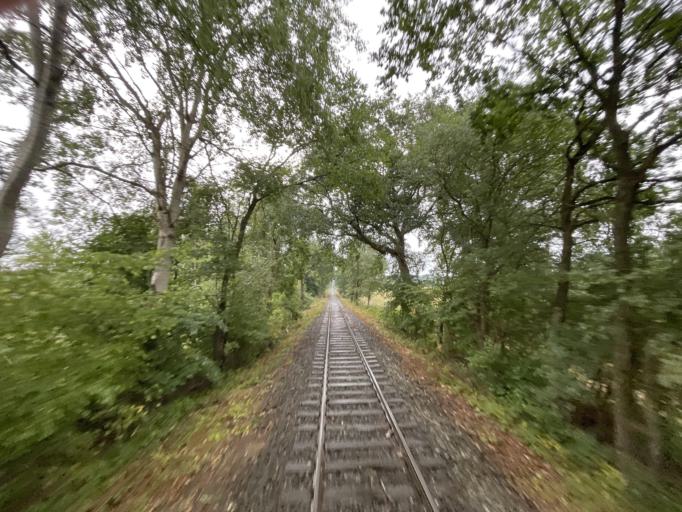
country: DE
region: Lower Saxony
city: Amelinghausen
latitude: 53.1295
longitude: 10.2424
